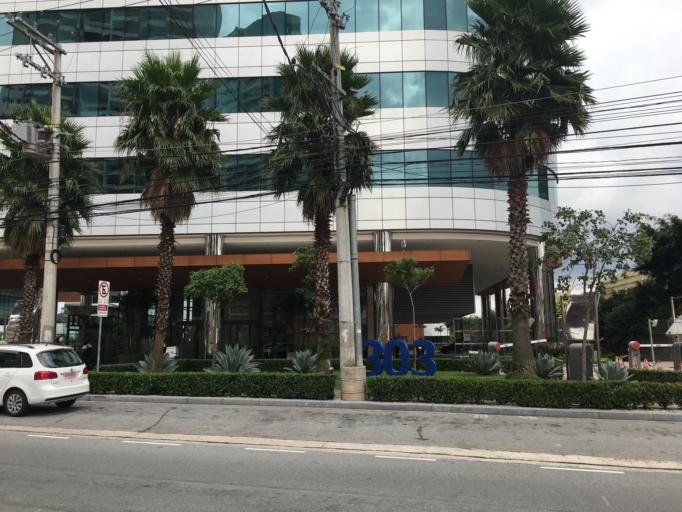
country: BR
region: Sao Paulo
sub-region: Sao Paulo
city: Sao Paulo
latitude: -23.5687
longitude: -46.7003
